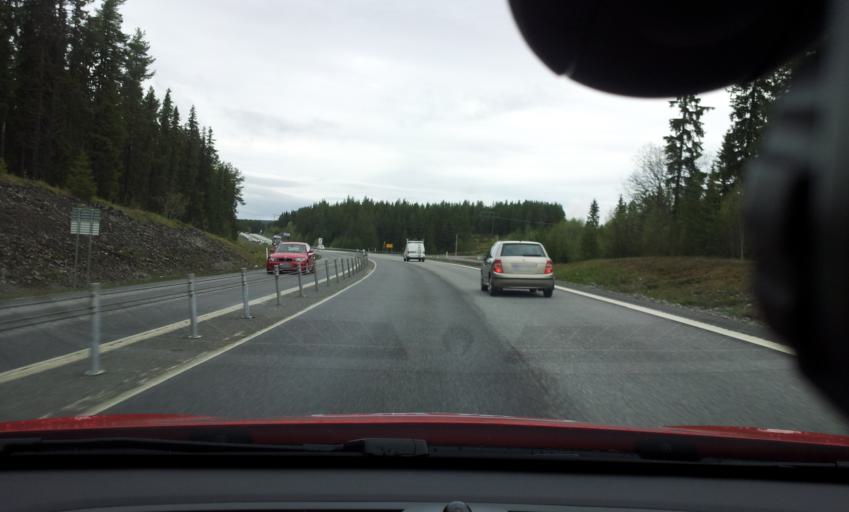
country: SE
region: Jaemtland
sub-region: OEstersunds Kommun
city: Brunflo
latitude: 63.1163
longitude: 14.7982
